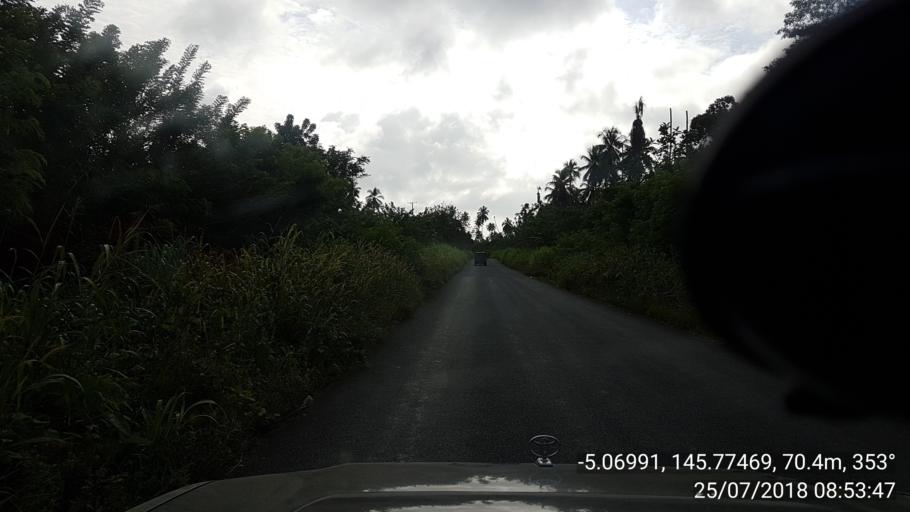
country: PG
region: Madang
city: Madang
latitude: -5.0700
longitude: 145.7747
